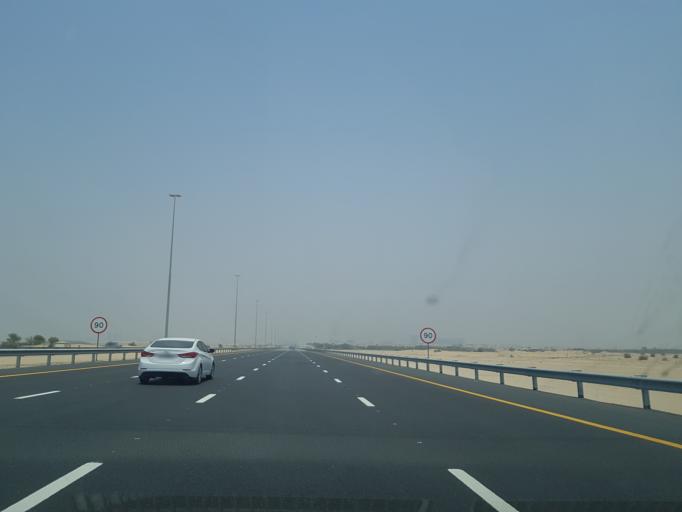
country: AE
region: Dubai
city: Dubai
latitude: 25.0770
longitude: 55.3335
